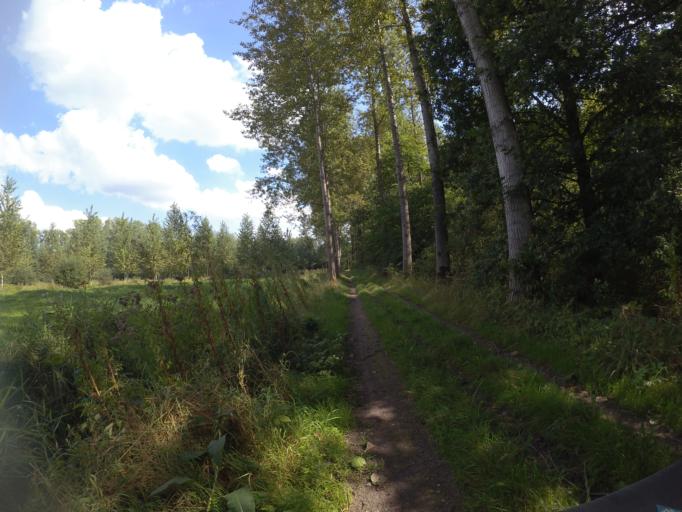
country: NL
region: North Brabant
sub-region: Gemeente Schijndel
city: Schijndel
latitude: 51.6383
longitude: 5.4574
